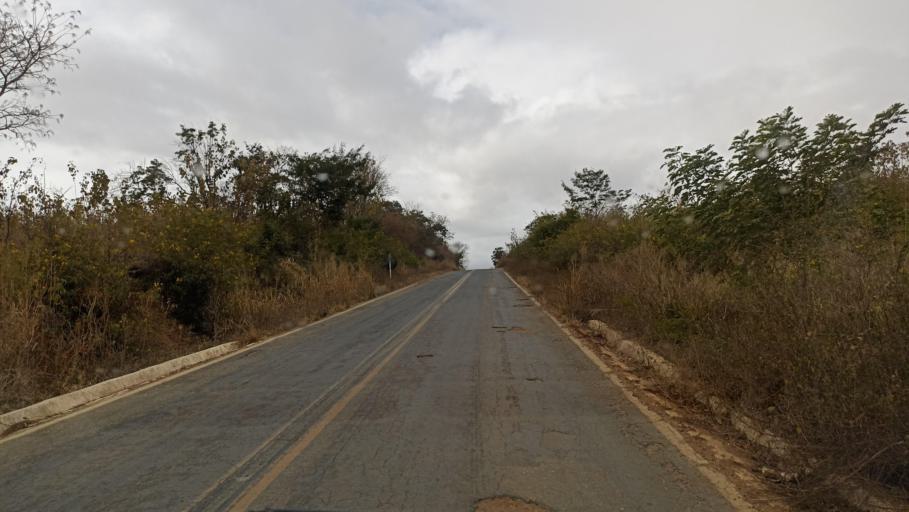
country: BR
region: Minas Gerais
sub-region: Itinga
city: Itinga
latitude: -16.6392
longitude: -41.8130
